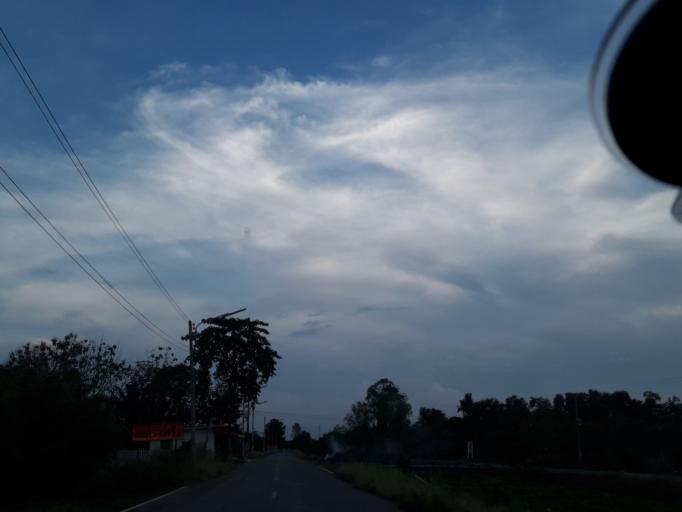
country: TH
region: Pathum Thani
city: Nong Suea
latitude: 14.2131
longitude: 100.8689
